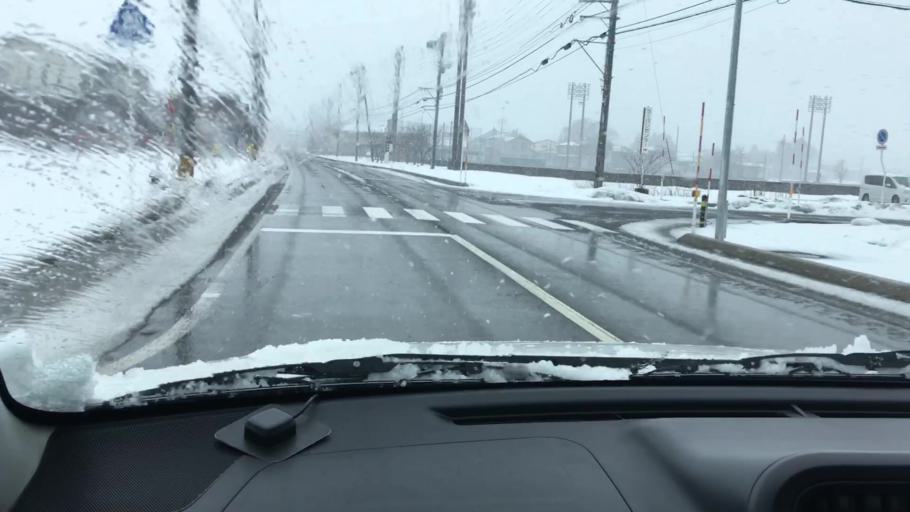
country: JP
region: Niigata
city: Joetsu
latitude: 37.0828
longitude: 138.2434
